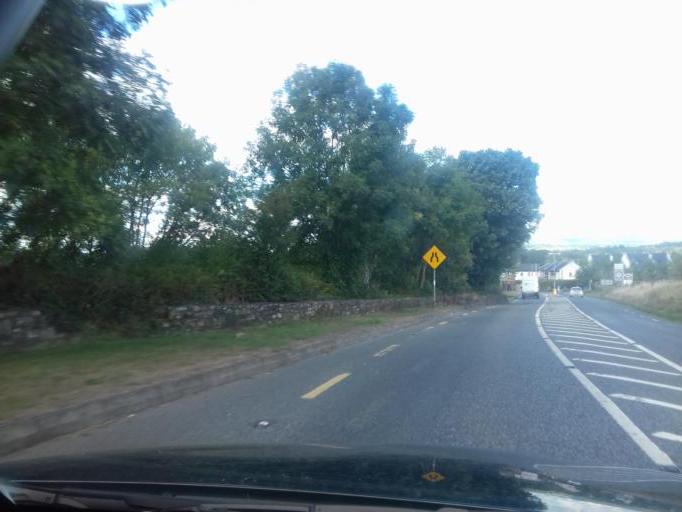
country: IE
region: Leinster
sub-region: Kilkenny
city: Thomastown
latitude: 52.5201
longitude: -7.1414
